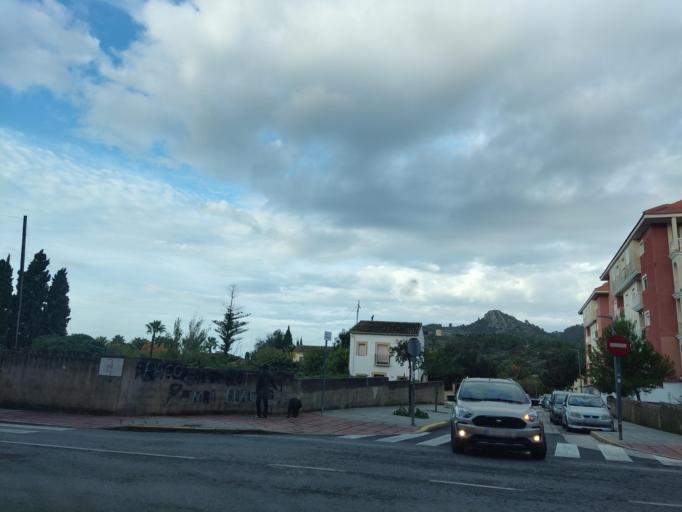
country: ES
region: Valencia
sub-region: Provincia de Alicante
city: Pedreguer
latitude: 38.7964
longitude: 0.0336
